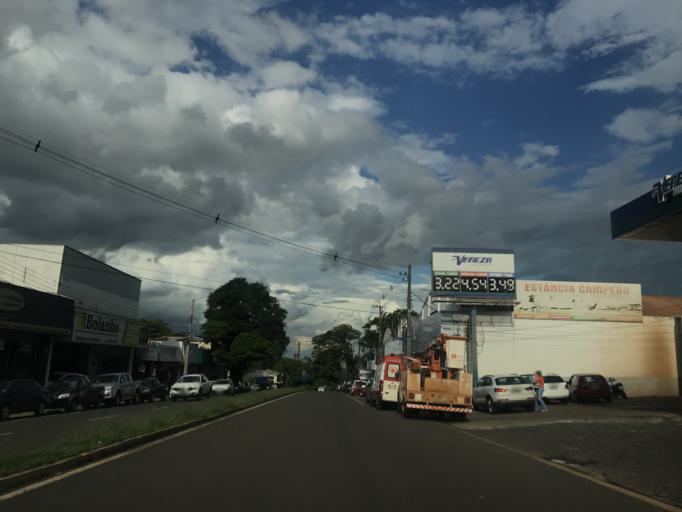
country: BR
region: Parana
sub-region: Maringa
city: Maringa
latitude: -23.4260
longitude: -51.9630
